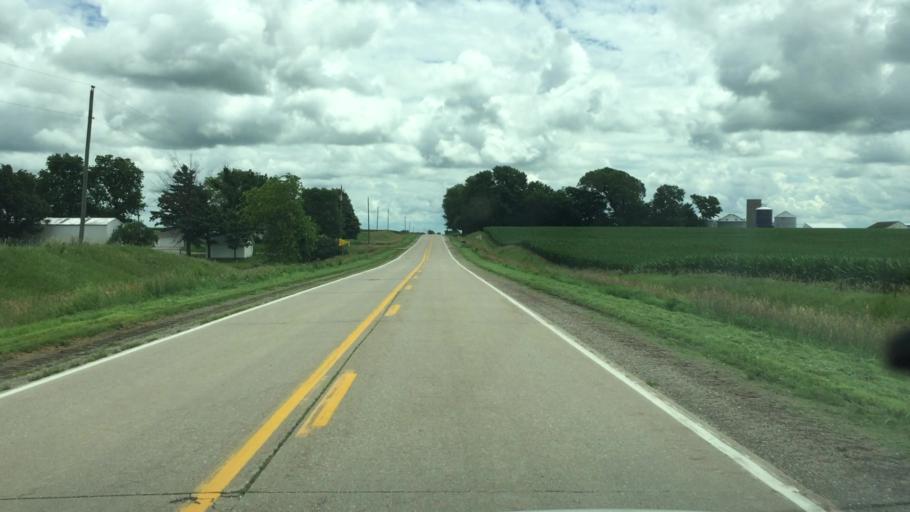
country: US
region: Iowa
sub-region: Jasper County
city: Monroe
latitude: 41.5807
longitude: -93.1452
